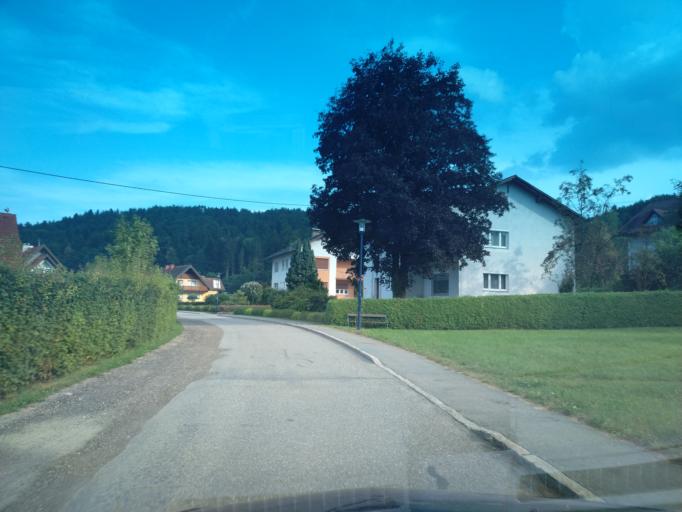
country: AT
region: Styria
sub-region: Politischer Bezirk Deutschlandsberg
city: Wies
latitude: 46.7173
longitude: 15.2738
